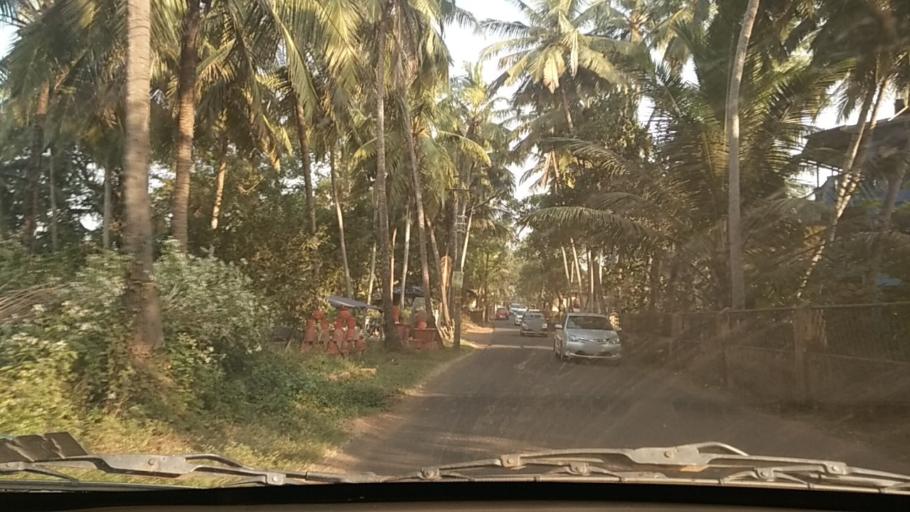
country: IN
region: Goa
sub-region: North Goa
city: Panaji
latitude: 15.4881
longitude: 73.8492
